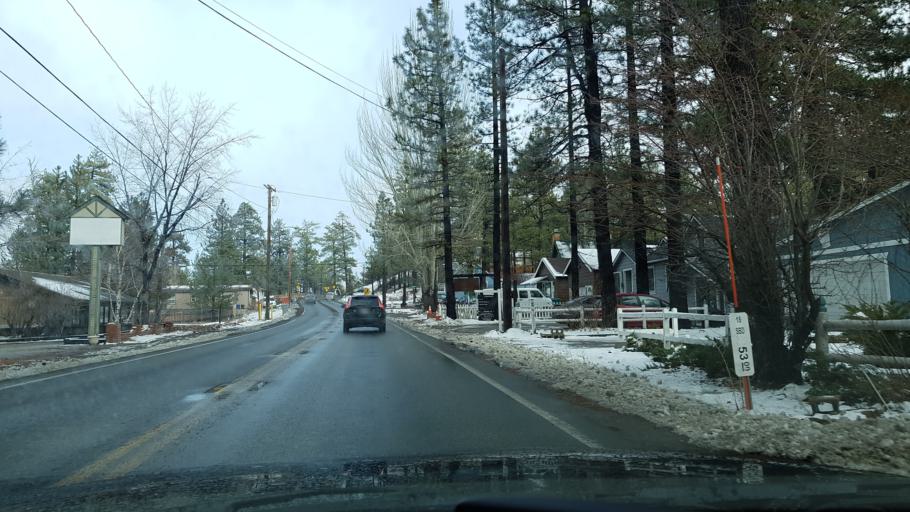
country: US
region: California
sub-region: San Bernardino County
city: Big Bear City
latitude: 34.2604
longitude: -116.8602
